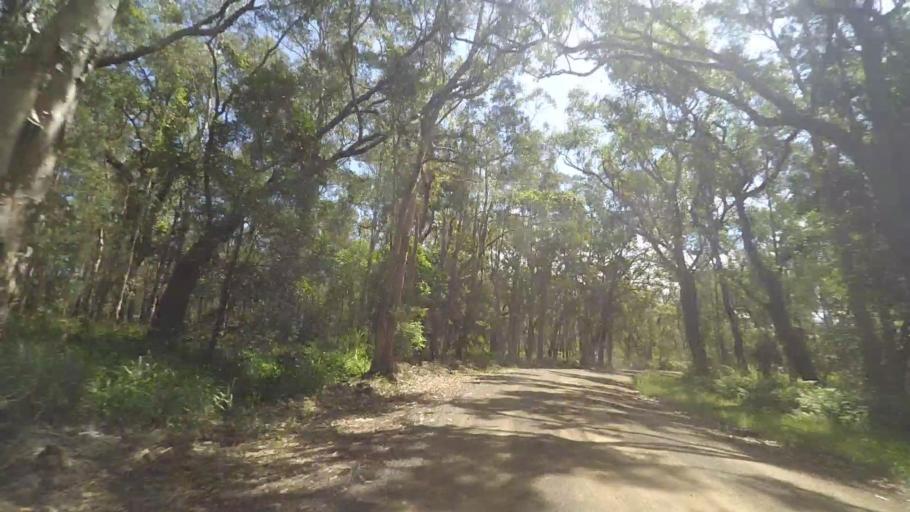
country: AU
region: New South Wales
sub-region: Great Lakes
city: Bulahdelah
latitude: -32.5099
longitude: 152.2930
